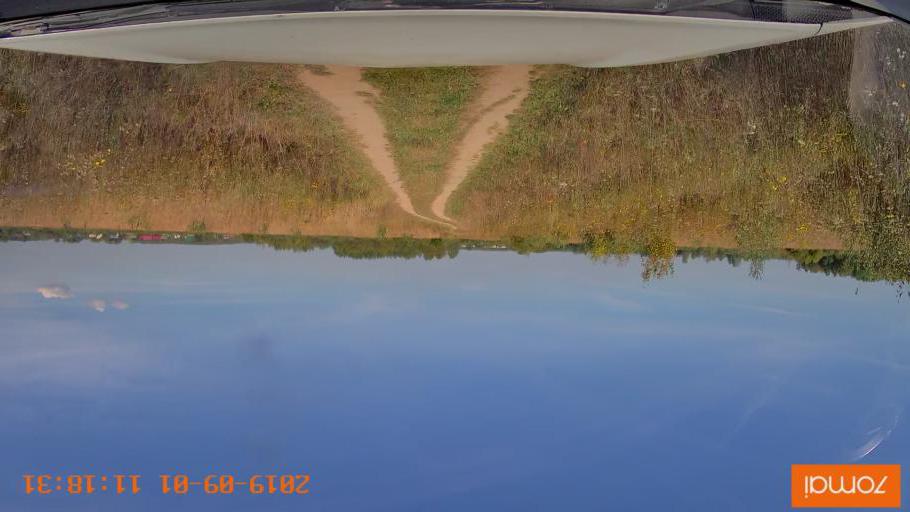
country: RU
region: Kaluga
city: Detchino
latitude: 54.8264
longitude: 36.3649
